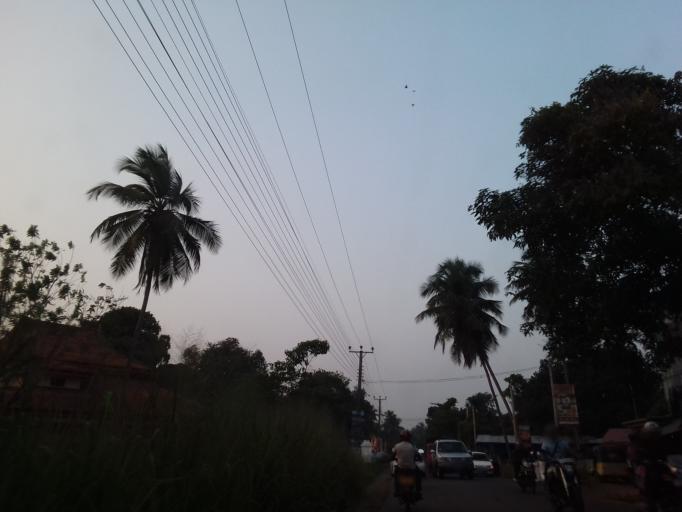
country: LK
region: Western
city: Welisara
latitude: 7.0432
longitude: 79.9574
